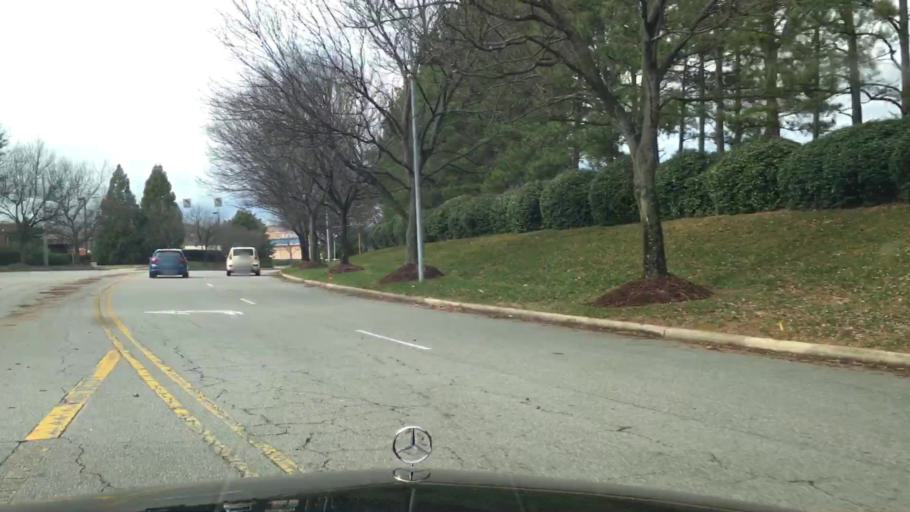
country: US
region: North Carolina
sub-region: Wake County
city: Cary
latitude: 35.7590
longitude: -78.7396
